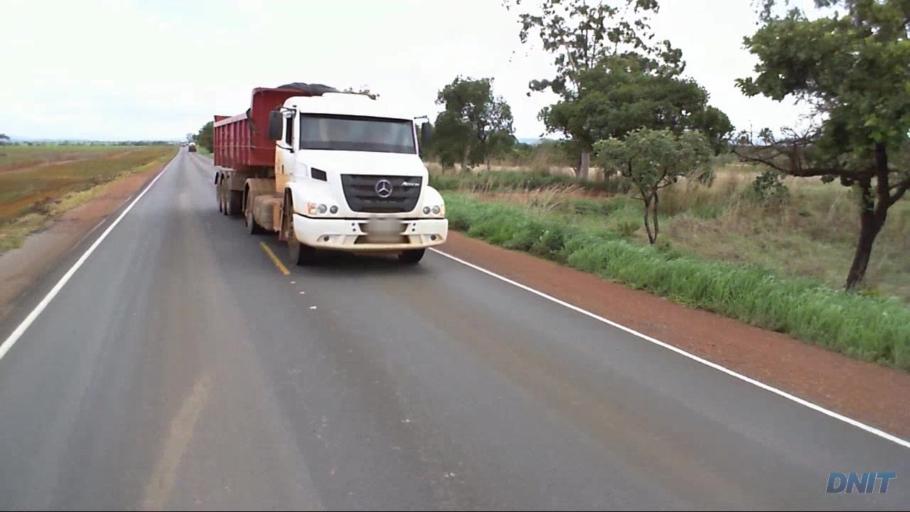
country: BR
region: Goias
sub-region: Padre Bernardo
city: Padre Bernardo
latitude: -15.3296
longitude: -48.2319
